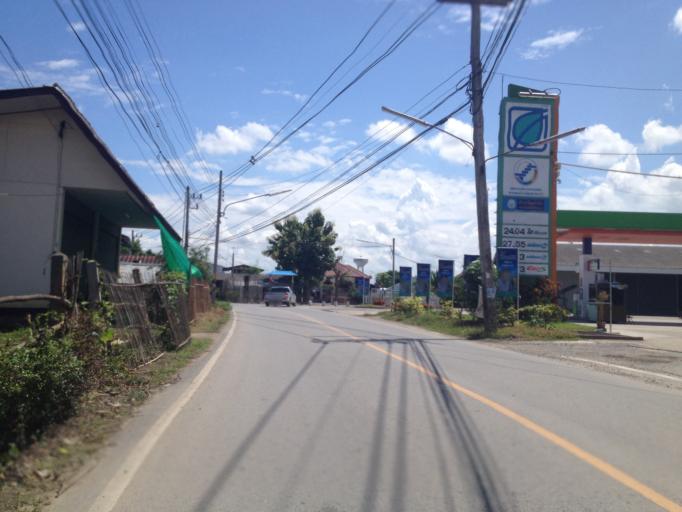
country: TH
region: Chiang Mai
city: Hang Dong
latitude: 18.6593
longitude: 98.9214
